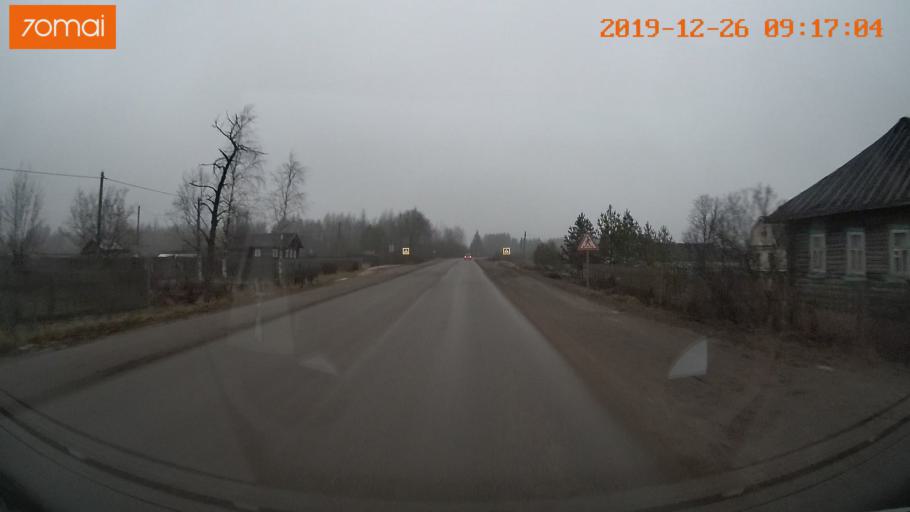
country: RU
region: Vologda
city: Gryazovets
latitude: 58.9256
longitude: 40.2389
